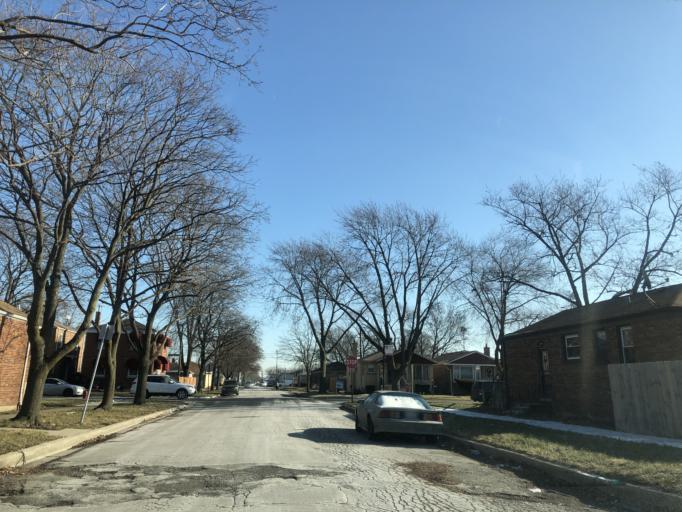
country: US
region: Illinois
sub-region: Cook County
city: Evergreen Park
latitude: 41.7591
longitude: -87.6872
